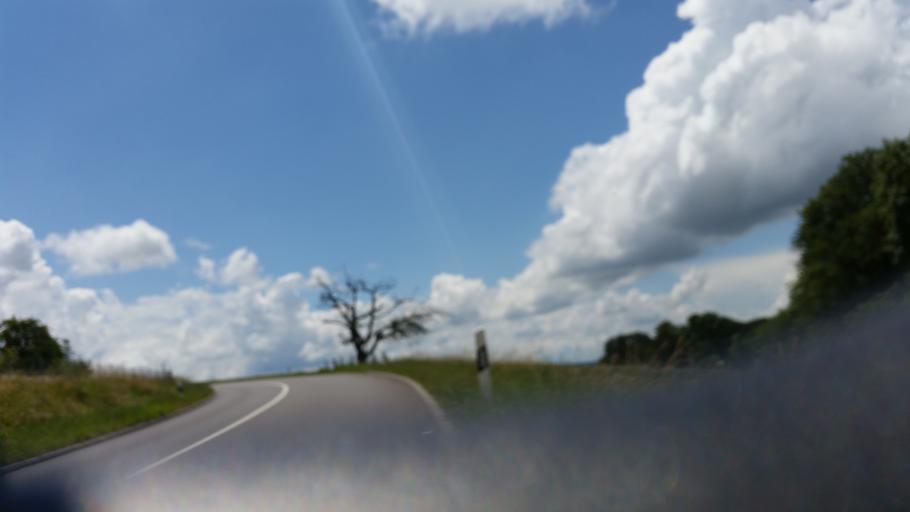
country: CH
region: Vaud
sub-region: Gros-de-Vaud District
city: Rueyres
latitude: 46.7303
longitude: 6.7402
